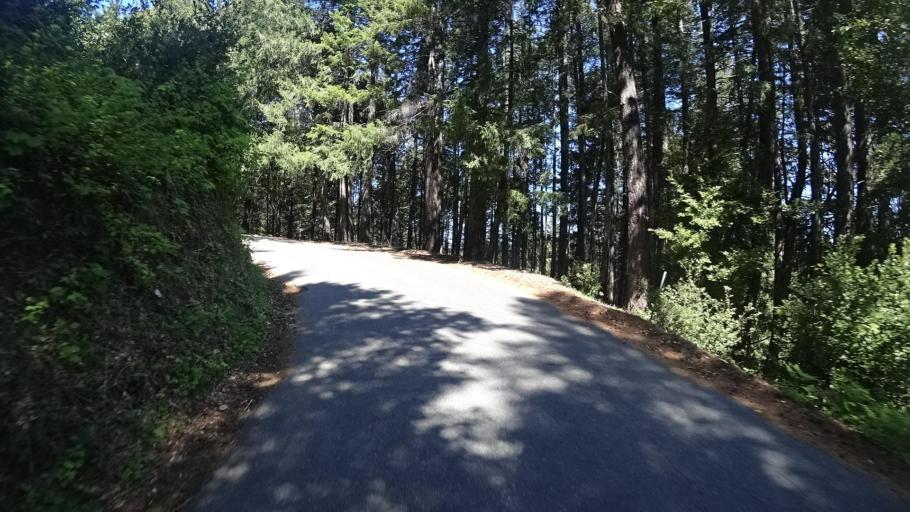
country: US
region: California
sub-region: Humboldt County
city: Redway
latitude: 40.1464
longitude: -124.0149
